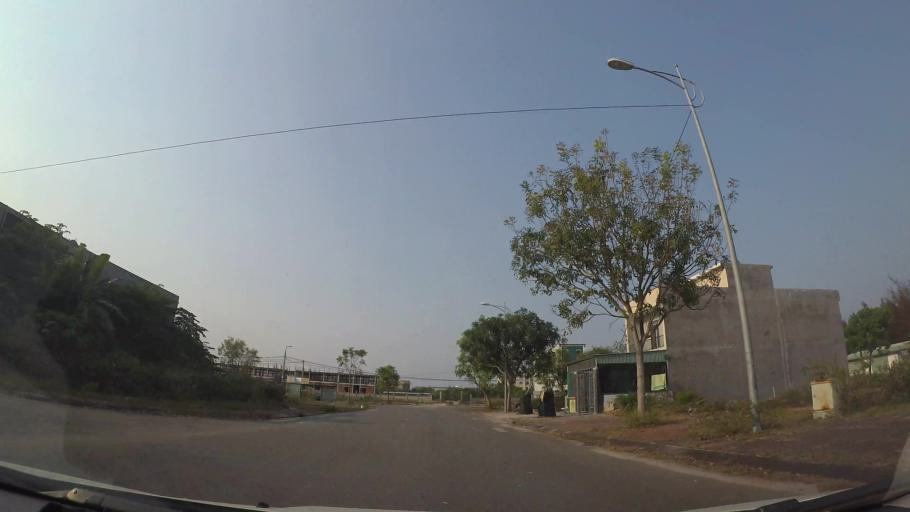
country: VN
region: Da Nang
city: Ngu Hanh Son
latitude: 15.9712
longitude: 108.2567
